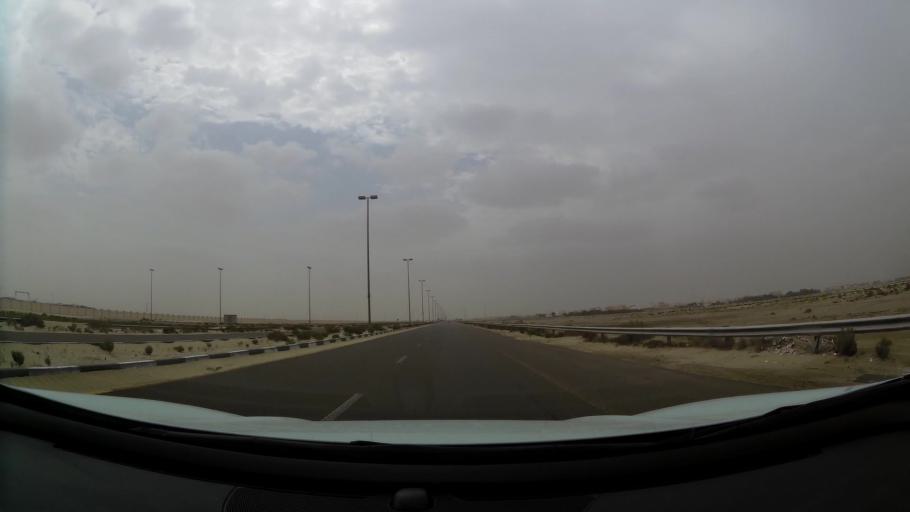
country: AE
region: Abu Dhabi
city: Abu Dhabi
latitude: 24.3813
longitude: 54.6770
